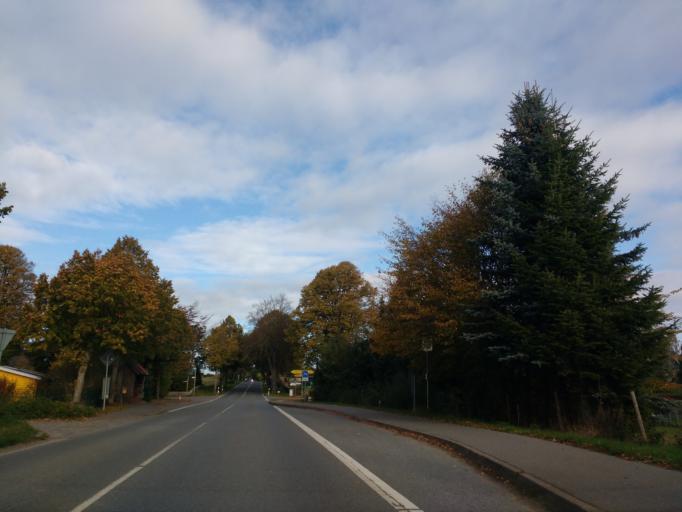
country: DE
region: Schleswig-Holstein
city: Altenkrempe
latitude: 54.1395
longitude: 10.8235
